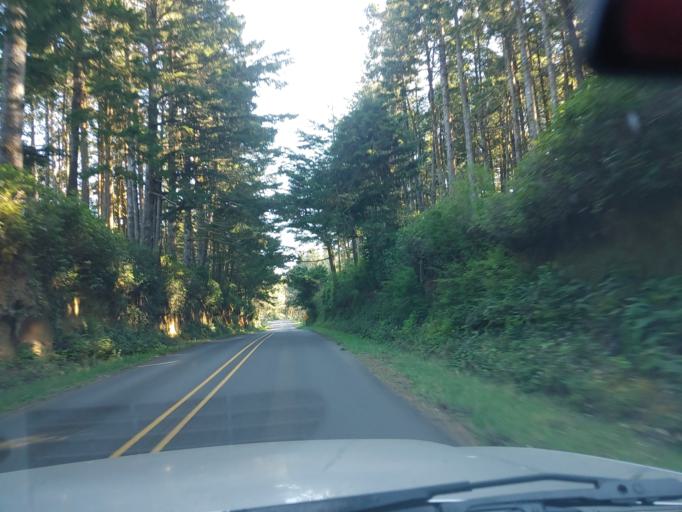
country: US
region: Oregon
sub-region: Lincoln County
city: Depoe Bay
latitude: 44.7435
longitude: -124.0559
